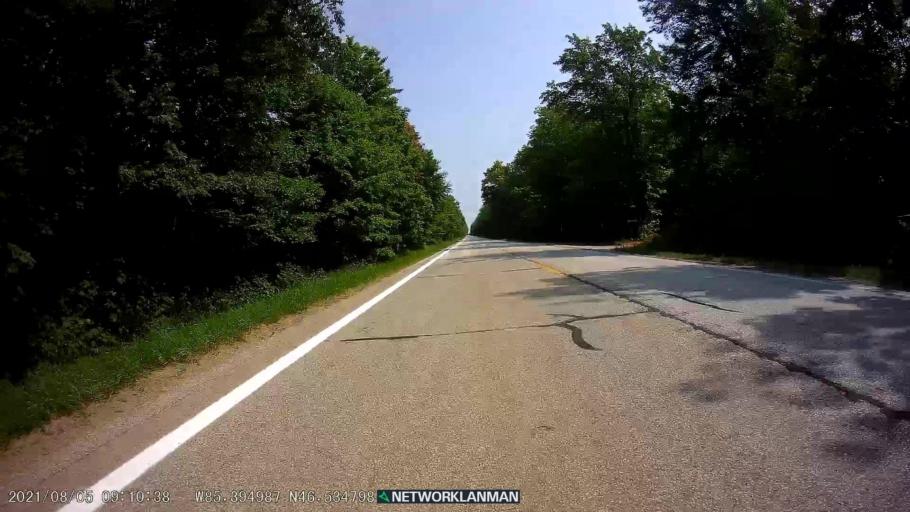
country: US
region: Michigan
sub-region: Luce County
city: Newberry
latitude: 46.5347
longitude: -85.3952
